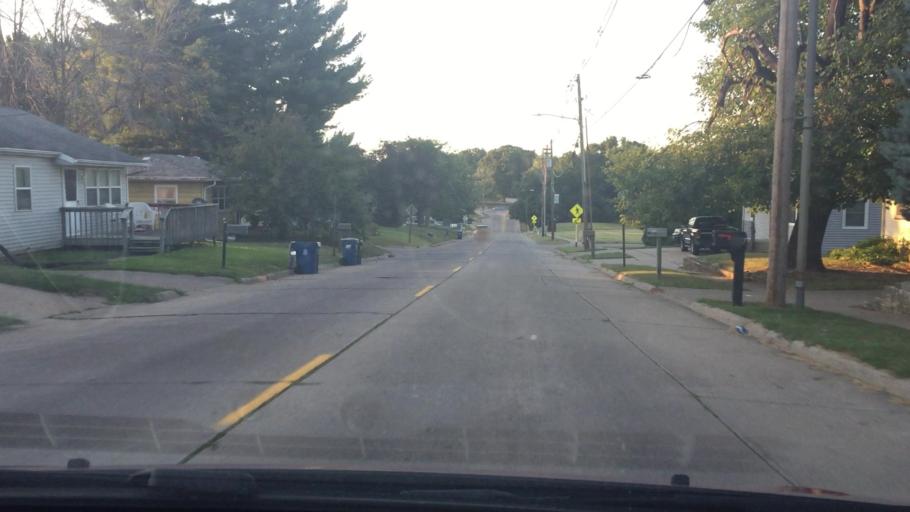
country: US
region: Iowa
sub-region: Muscatine County
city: Muscatine
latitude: 41.4325
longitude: -91.0649
